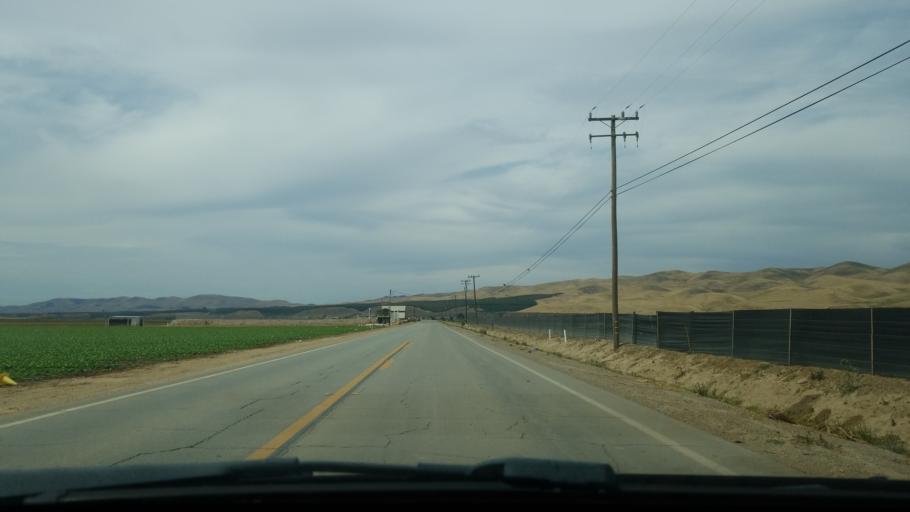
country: US
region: California
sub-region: Santa Barbara County
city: Santa Maria
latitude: 34.9140
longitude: -120.3478
